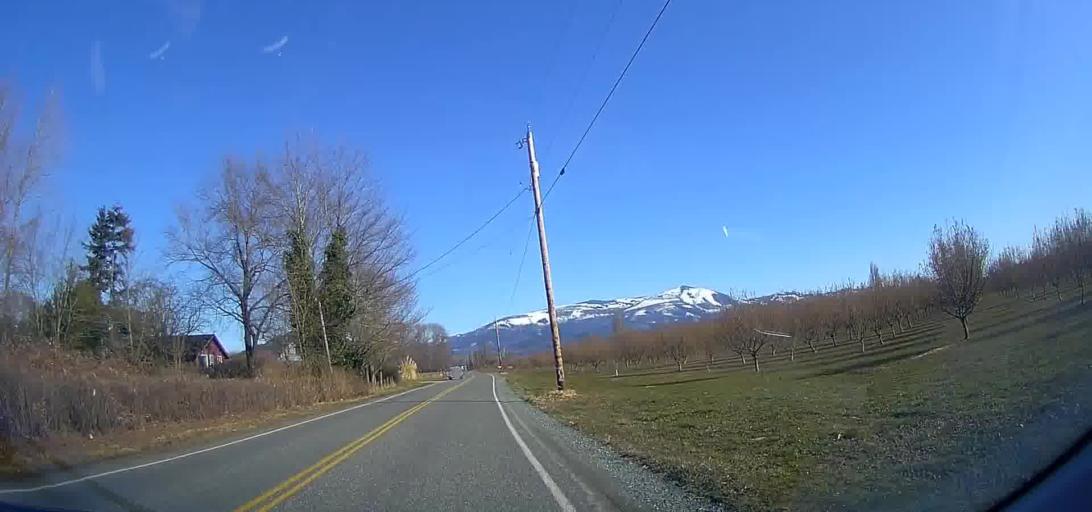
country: US
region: Washington
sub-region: Skagit County
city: Burlington
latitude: 48.4680
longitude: -122.2870
